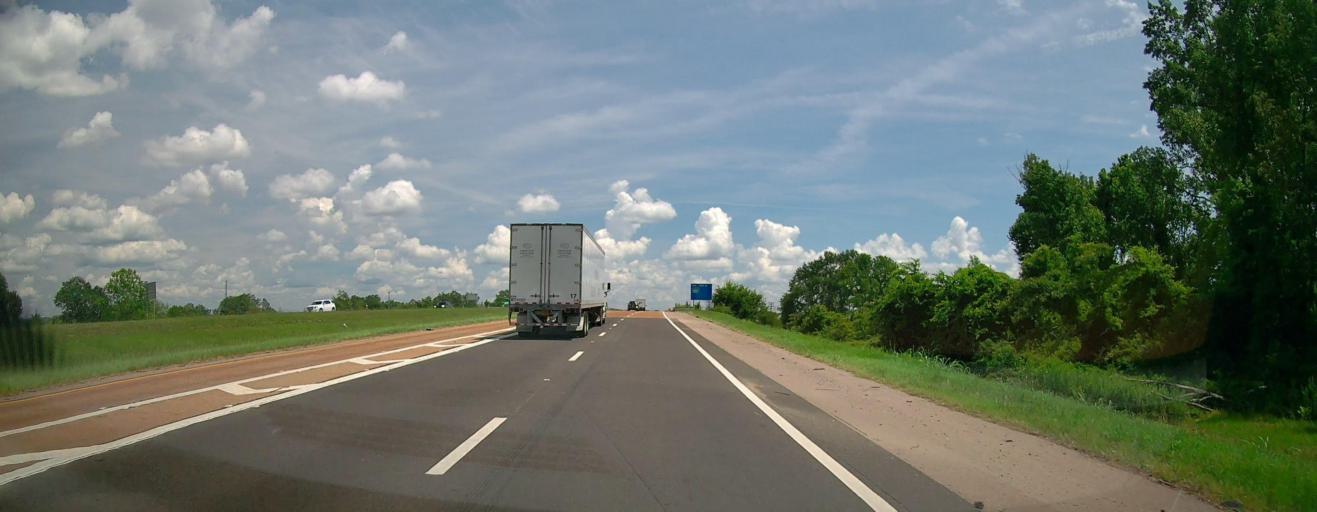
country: US
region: Mississippi
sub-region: Lee County
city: Tupelo
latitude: 34.2729
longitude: -88.7031
